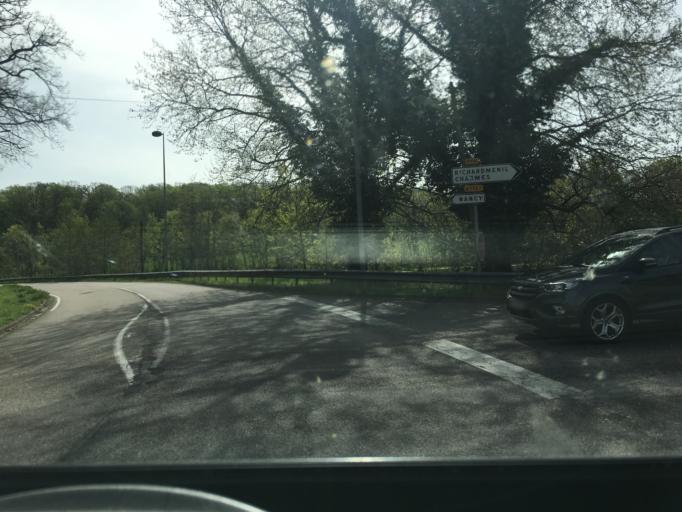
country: FR
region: Lorraine
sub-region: Departement de Meurthe-et-Moselle
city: Mereville
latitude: 48.6028
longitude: 6.1556
